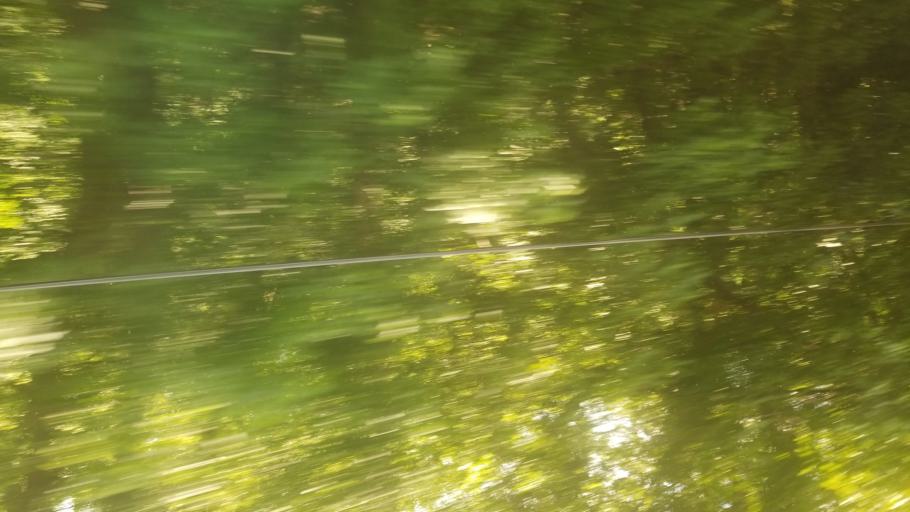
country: US
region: Maryland
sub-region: Frederick County
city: Point of Rocks
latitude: 39.2830
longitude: -77.5485
